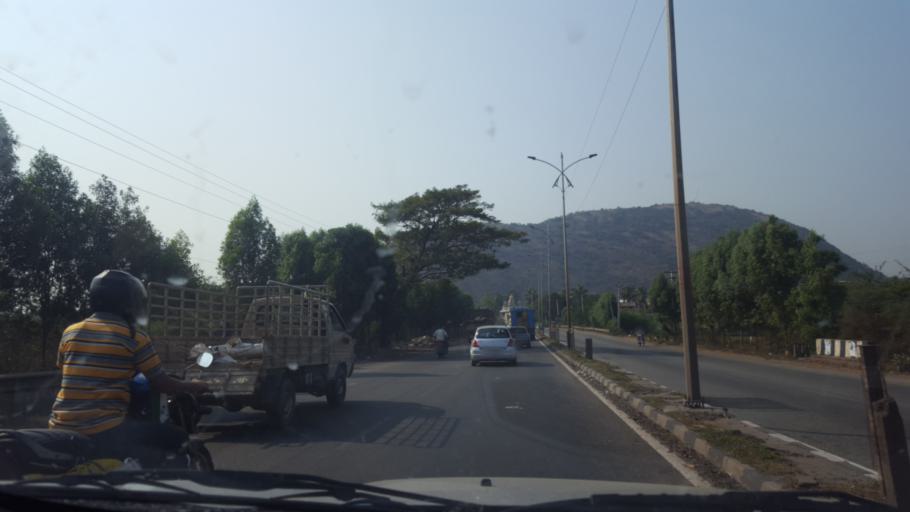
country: IN
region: Andhra Pradesh
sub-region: Vishakhapatnam
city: Anakapalle
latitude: 17.6880
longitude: 83.0770
